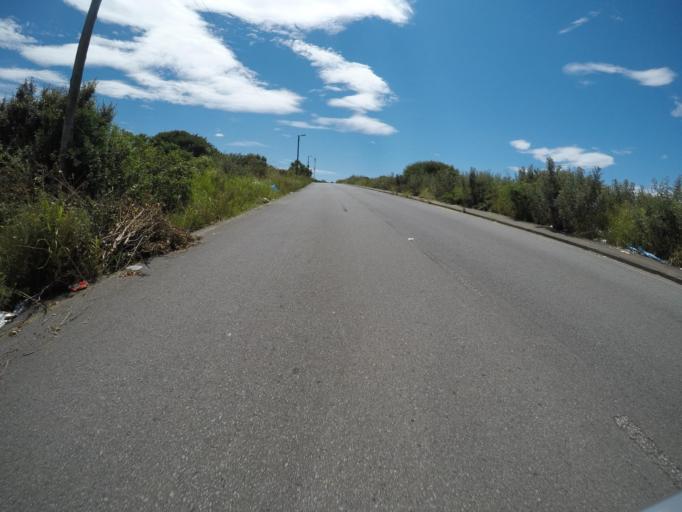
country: ZA
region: Eastern Cape
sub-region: Buffalo City Metropolitan Municipality
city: East London
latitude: -33.0406
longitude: 27.8674
